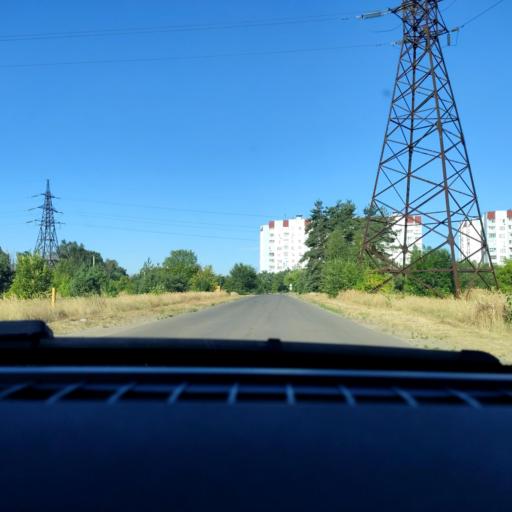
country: RU
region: Voronezj
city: Somovo
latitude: 51.7347
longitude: 39.2989
